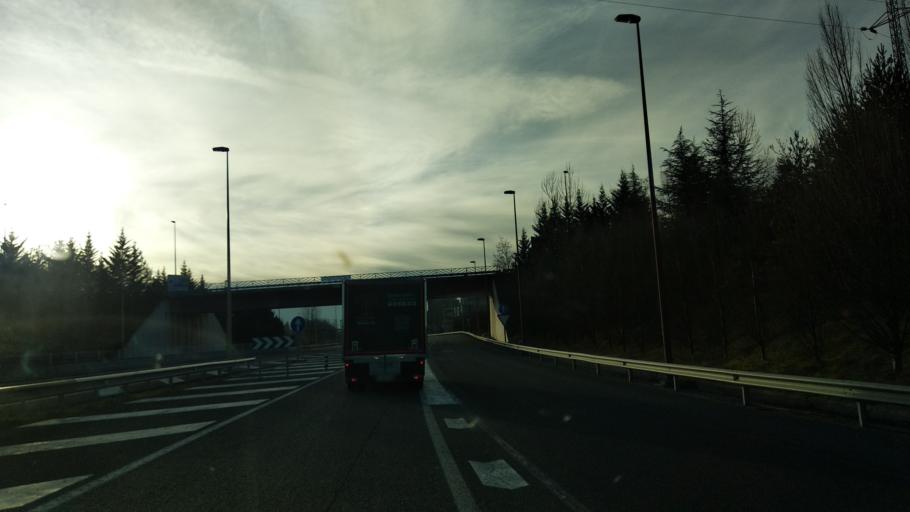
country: ES
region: Navarre
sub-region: Provincia de Navarra
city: Olazagutia
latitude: 42.8844
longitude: -2.1819
